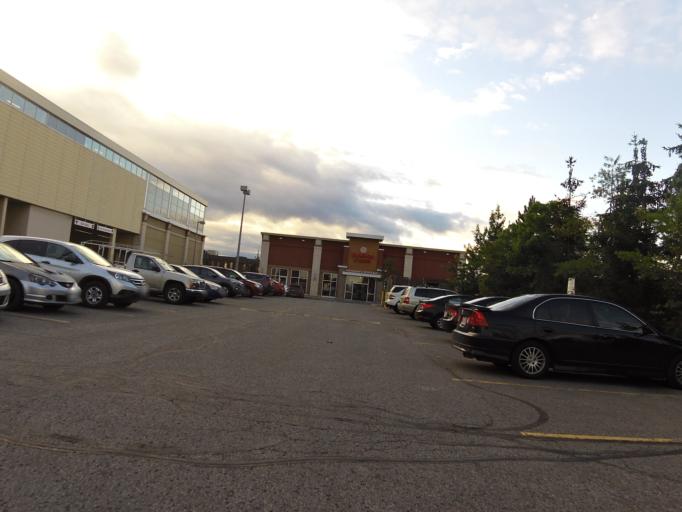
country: CA
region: Ontario
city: Ottawa
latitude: 45.3790
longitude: -75.7478
